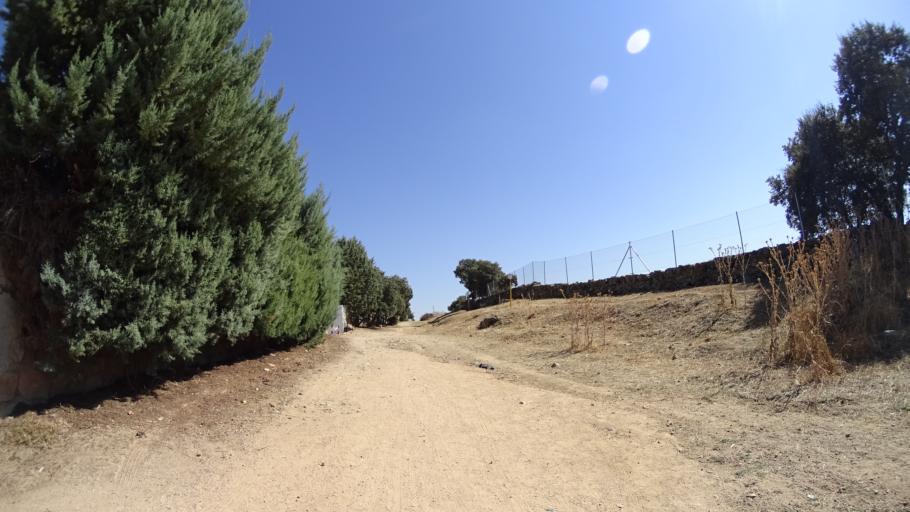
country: ES
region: Madrid
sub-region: Provincia de Madrid
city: Collado-Villalba
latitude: 40.6133
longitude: -4.0145
